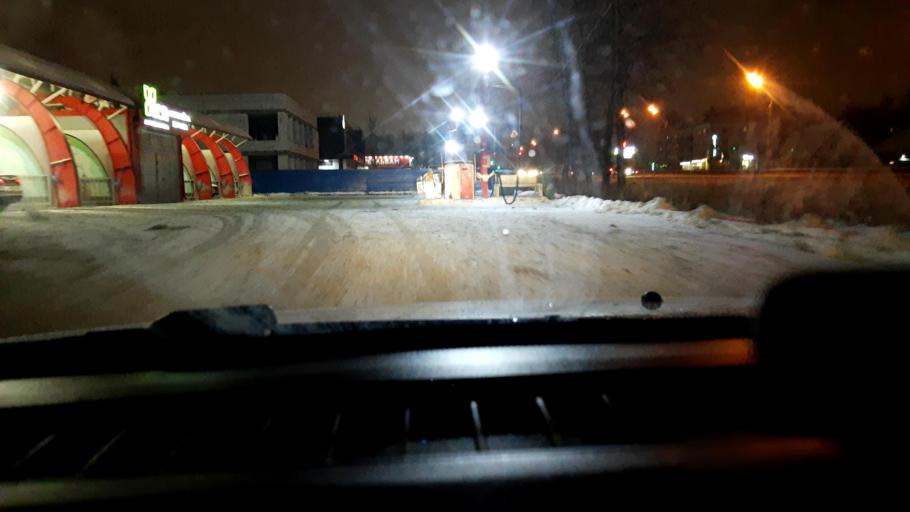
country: RU
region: Nizjnij Novgorod
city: Kstovo
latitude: 56.1583
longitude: 44.1966
